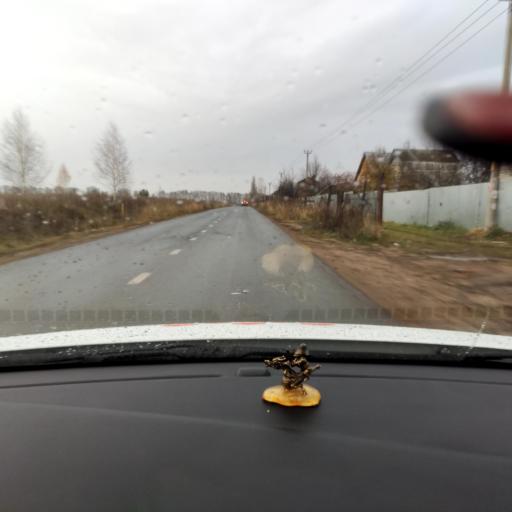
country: RU
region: Tatarstan
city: Vysokaya Gora
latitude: 55.8298
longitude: 49.2301
